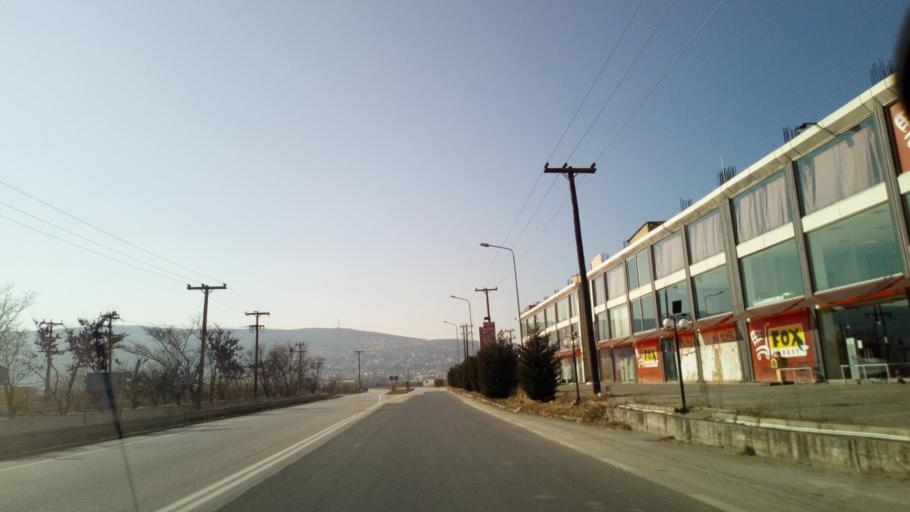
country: GR
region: Central Macedonia
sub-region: Nomos Thessalonikis
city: Lagyna
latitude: 40.7320
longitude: 23.0221
